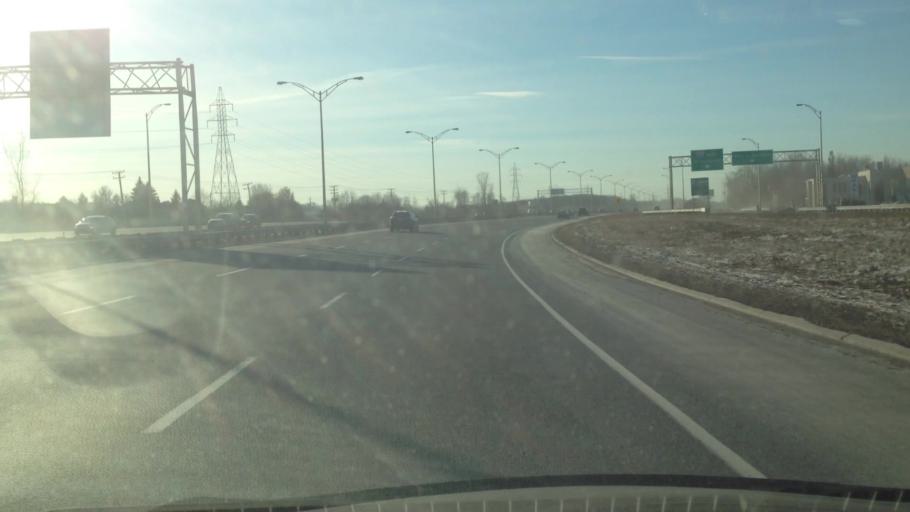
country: CA
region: Quebec
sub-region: Laurentides
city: Boisbriand
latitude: 45.6172
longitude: -73.8506
